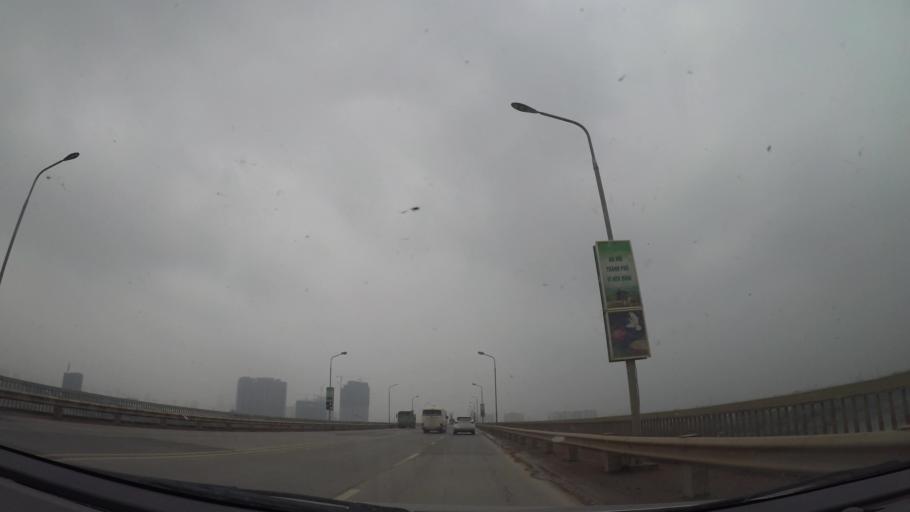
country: VN
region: Ha Noi
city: Tay Ho
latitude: 21.0968
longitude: 105.7863
